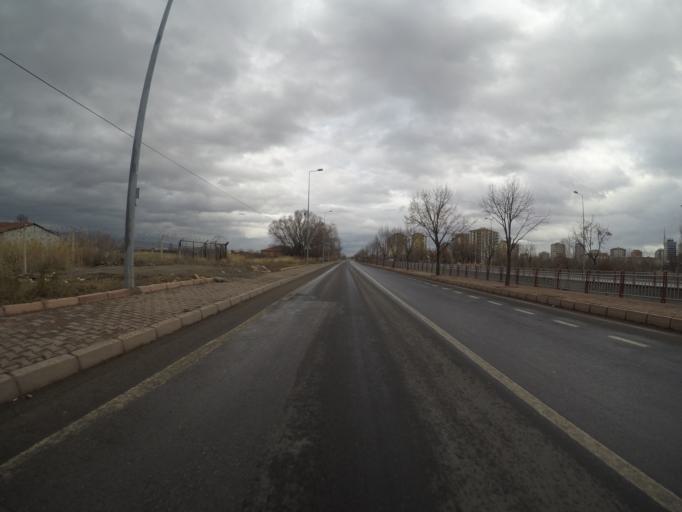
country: TR
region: Kayseri
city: Kayseri
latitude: 38.7559
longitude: 35.4788
